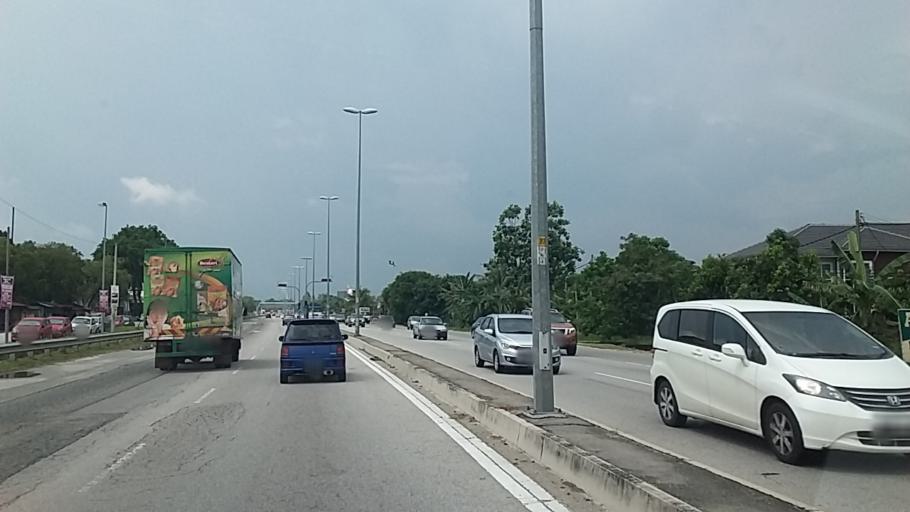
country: MY
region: Johor
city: Parit Raja
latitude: 1.8547
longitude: 103.0935
